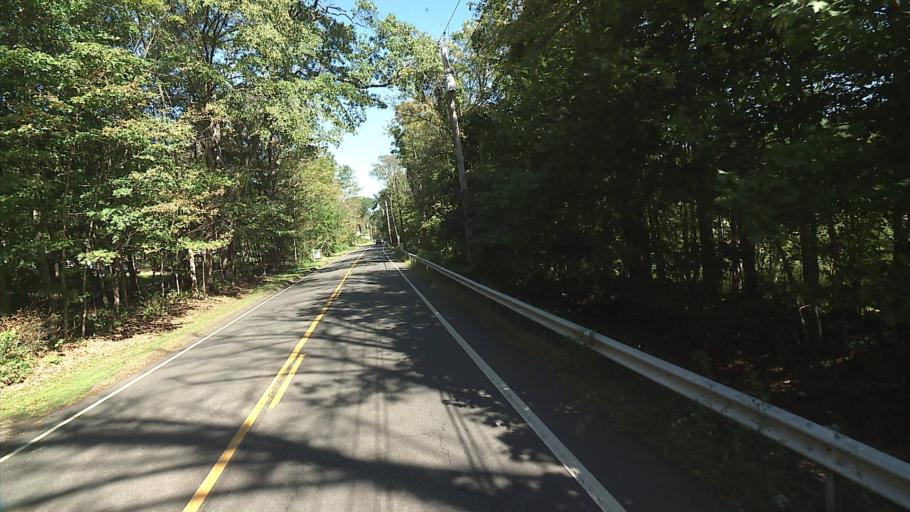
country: US
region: Connecticut
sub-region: New Haven County
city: Woodbridge
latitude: 41.3540
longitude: -72.9841
